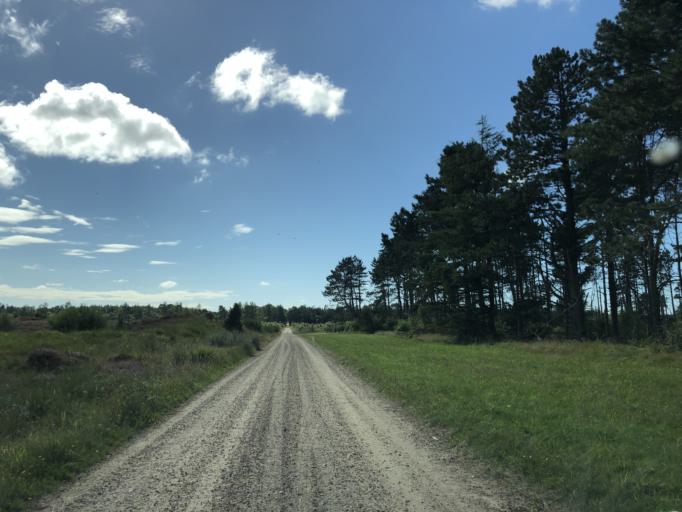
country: DK
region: Central Jutland
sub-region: Holstebro Kommune
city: Ulfborg
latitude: 56.2273
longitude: 8.4781
